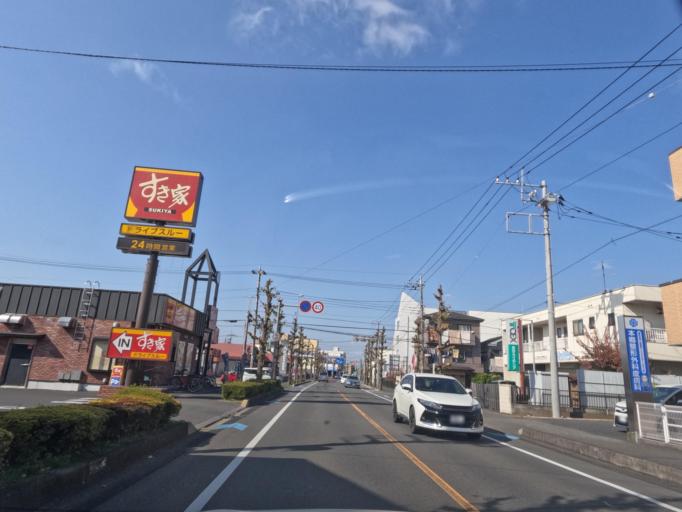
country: JP
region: Saitama
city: Ageoshimo
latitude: 35.9440
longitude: 139.6244
